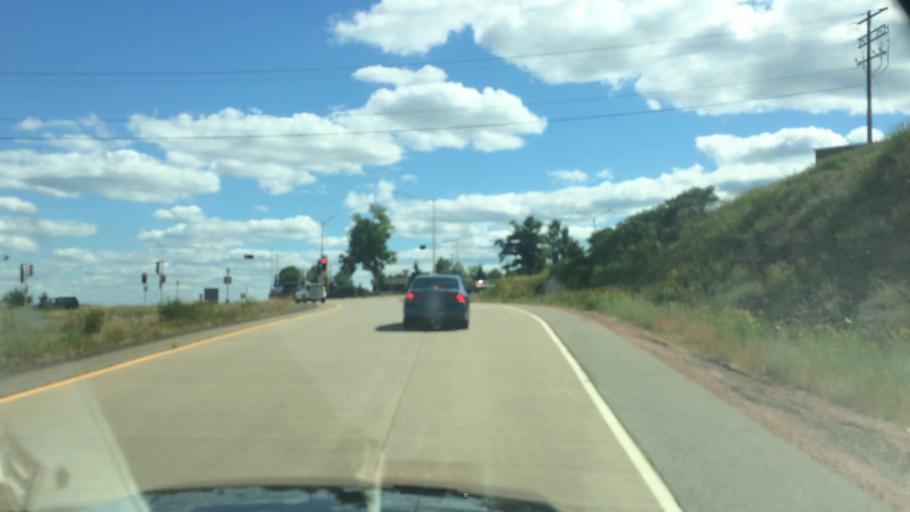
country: US
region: Wisconsin
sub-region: Marathon County
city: Wausau
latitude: 44.9703
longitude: -89.6573
